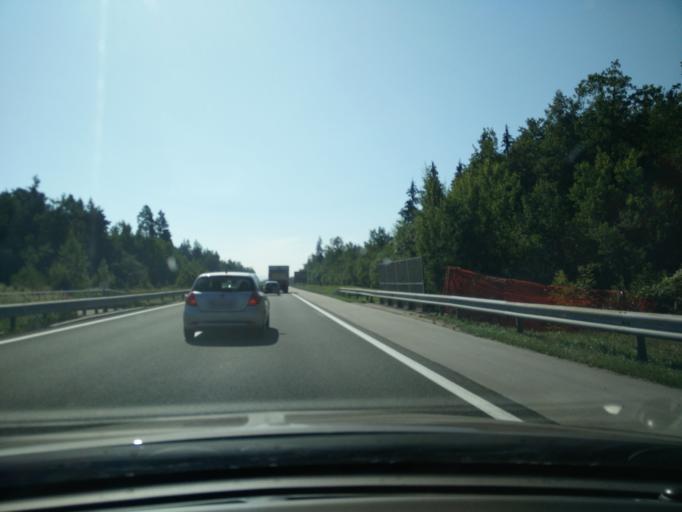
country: SI
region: Kranj
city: Britof
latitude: 46.2491
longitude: 14.3903
